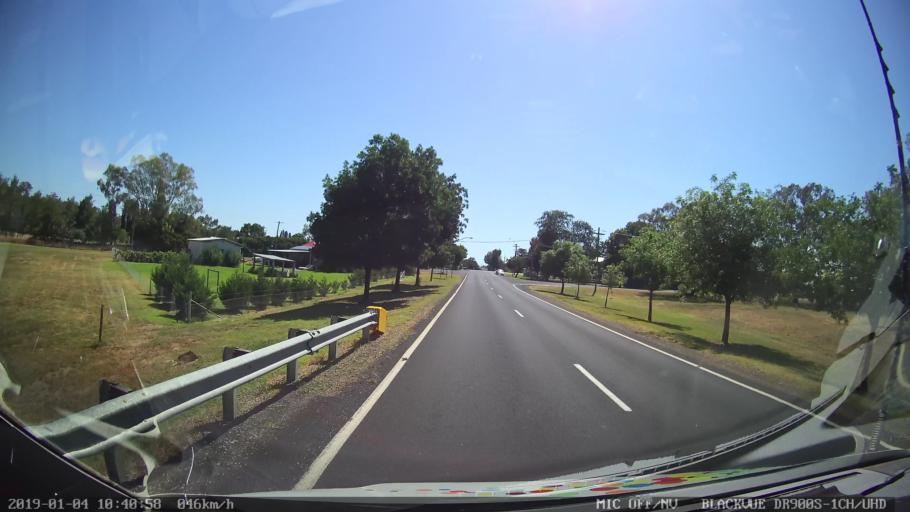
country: AU
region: New South Wales
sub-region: Cabonne
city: Molong
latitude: -33.2880
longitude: 148.7358
